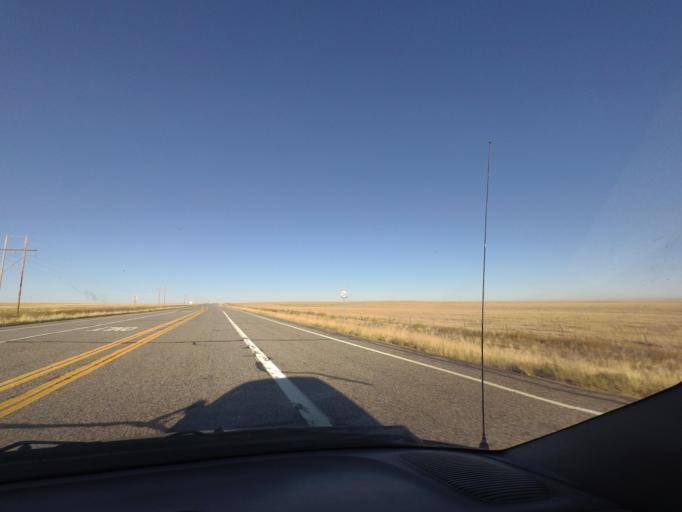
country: US
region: Colorado
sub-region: Lincoln County
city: Limon
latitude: 39.7399
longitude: -103.5190
